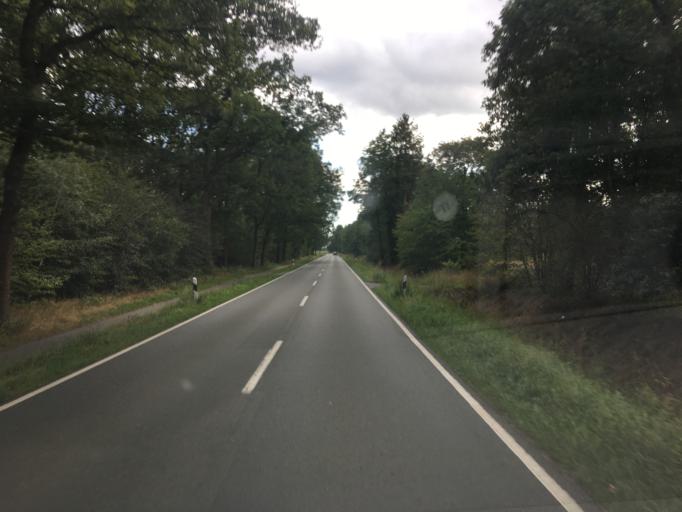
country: DE
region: Lower Saxony
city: Friesoythe
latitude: 53.0656
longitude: 7.8478
